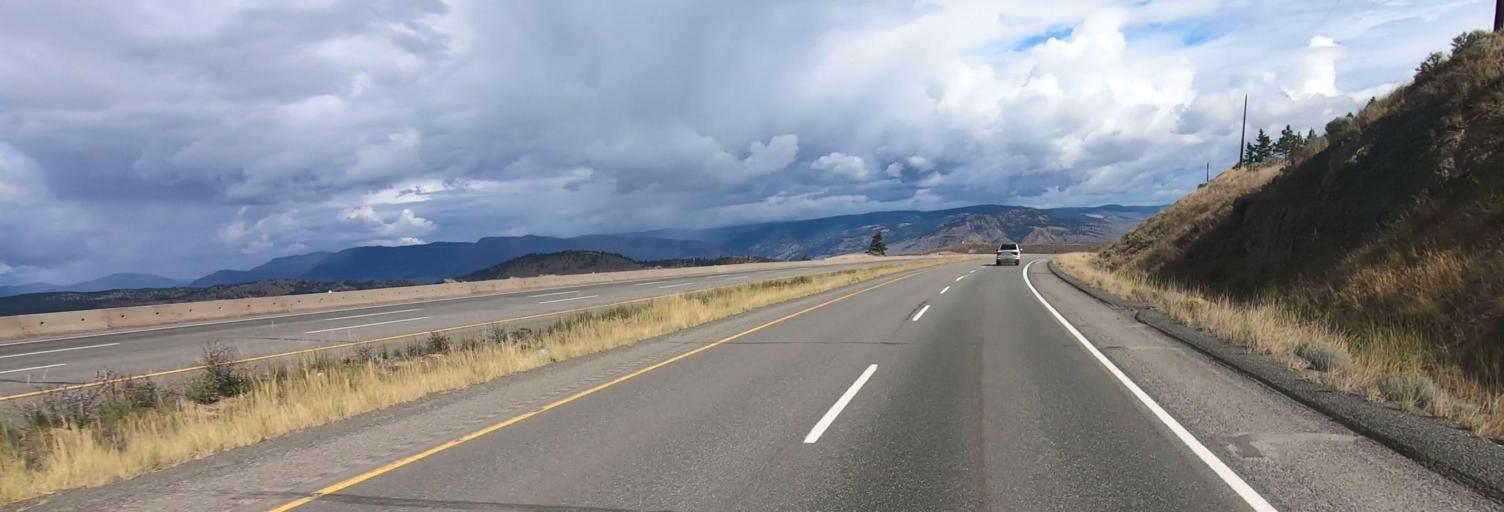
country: CA
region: British Columbia
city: Kamloops
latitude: 50.6475
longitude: -120.4861
